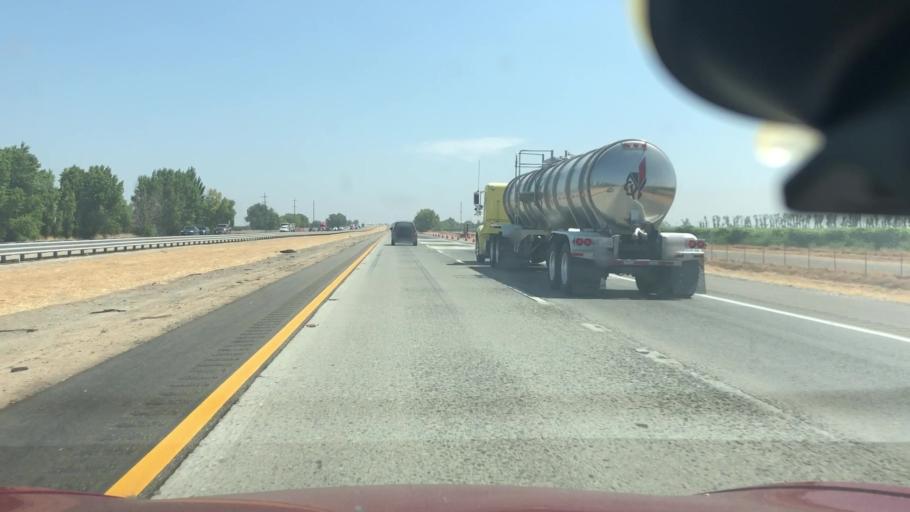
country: US
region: California
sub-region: San Joaquin County
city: Thornton
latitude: 38.1986
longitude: -121.4115
